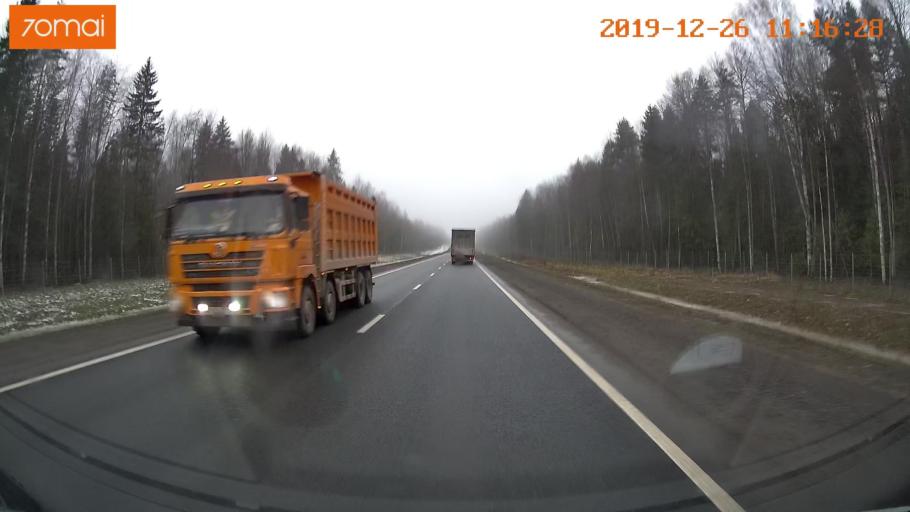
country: RU
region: Vologda
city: Chebsara
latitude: 59.1201
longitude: 39.0796
